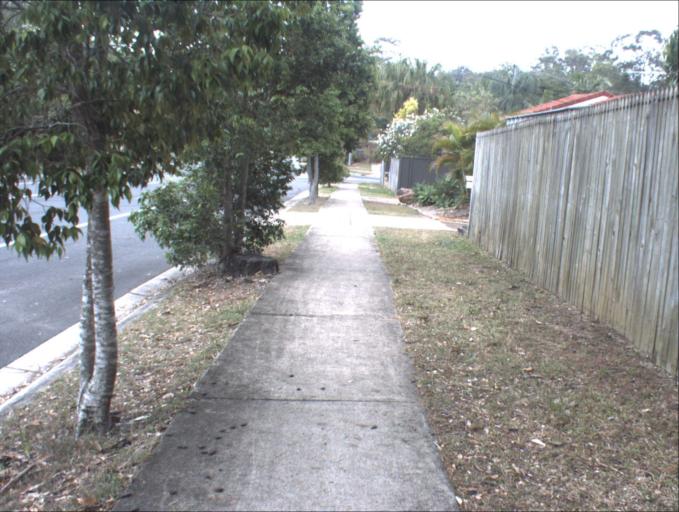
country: AU
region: Queensland
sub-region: Logan
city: Beenleigh
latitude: -27.6768
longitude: 153.1819
